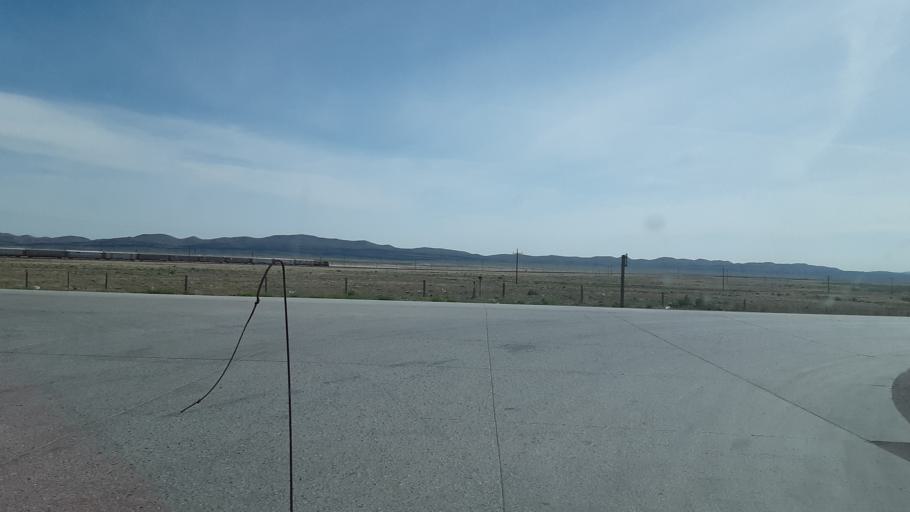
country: US
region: Wyoming
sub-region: Carbon County
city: Rawlins
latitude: 41.7739
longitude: -107.0839
